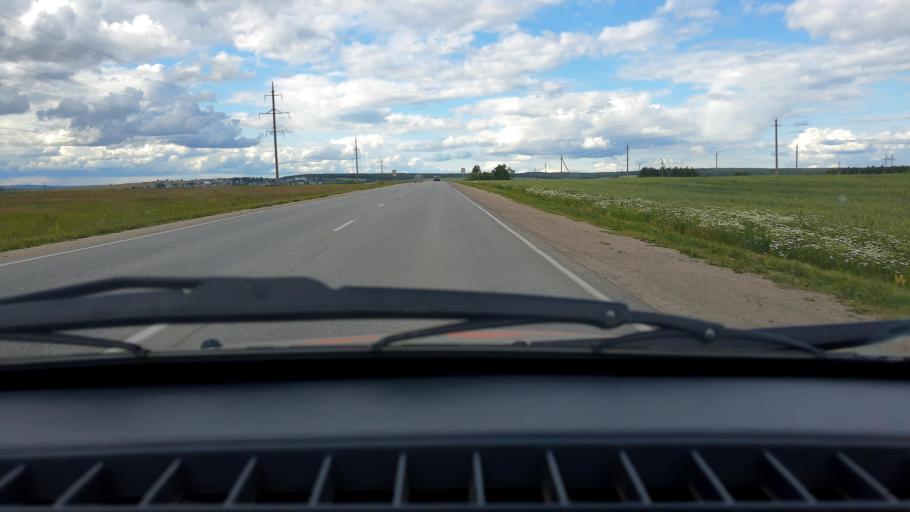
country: RU
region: Bashkortostan
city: Iglino
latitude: 54.8912
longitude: 56.4722
